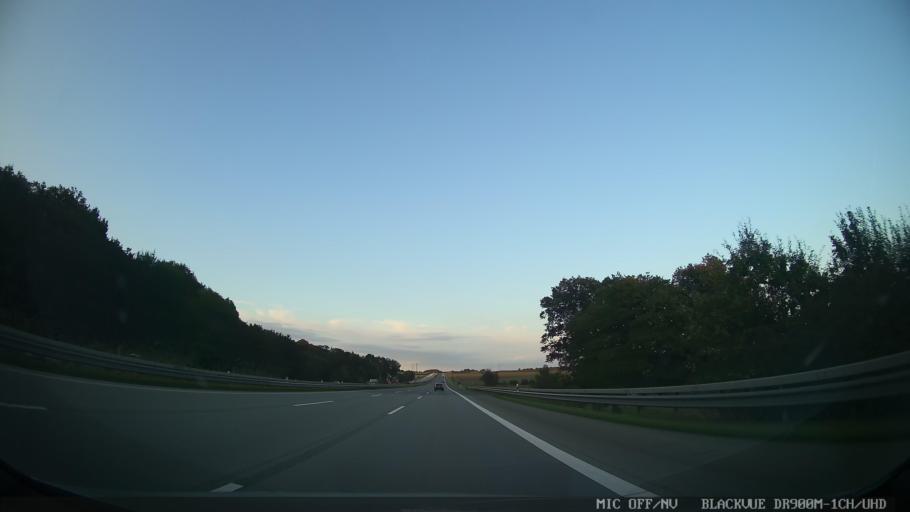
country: DE
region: Schleswig-Holstein
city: Lasbek
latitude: 53.7508
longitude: 10.3692
